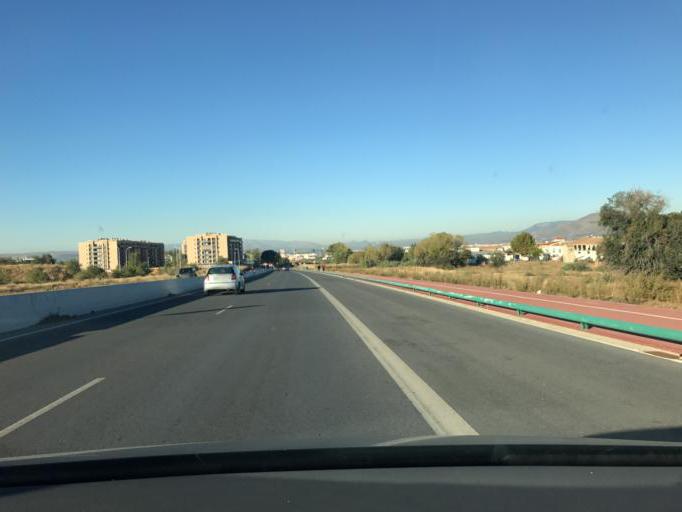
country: ES
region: Andalusia
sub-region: Provincia de Granada
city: Pulianas
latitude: 37.2134
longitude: -3.6046
